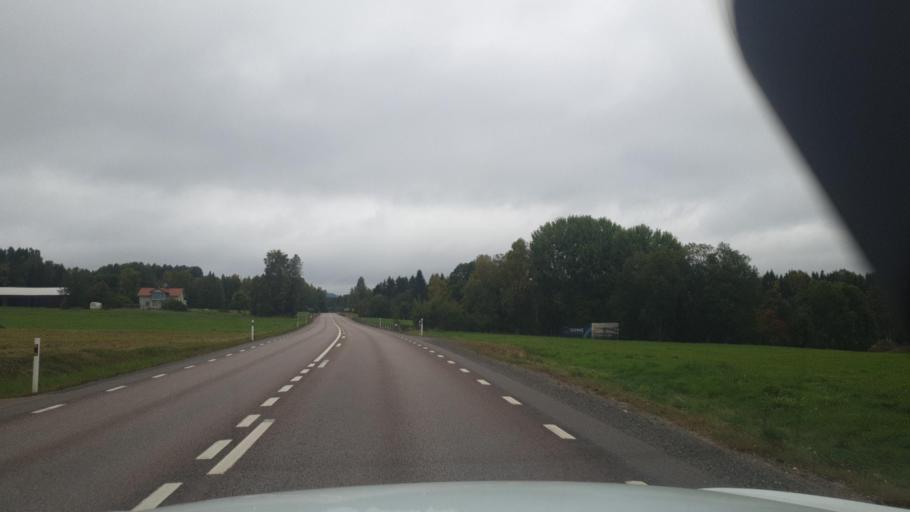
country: SE
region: Vaermland
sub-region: Sunne Kommun
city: Sunne
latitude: 59.7833
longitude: 13.0984
